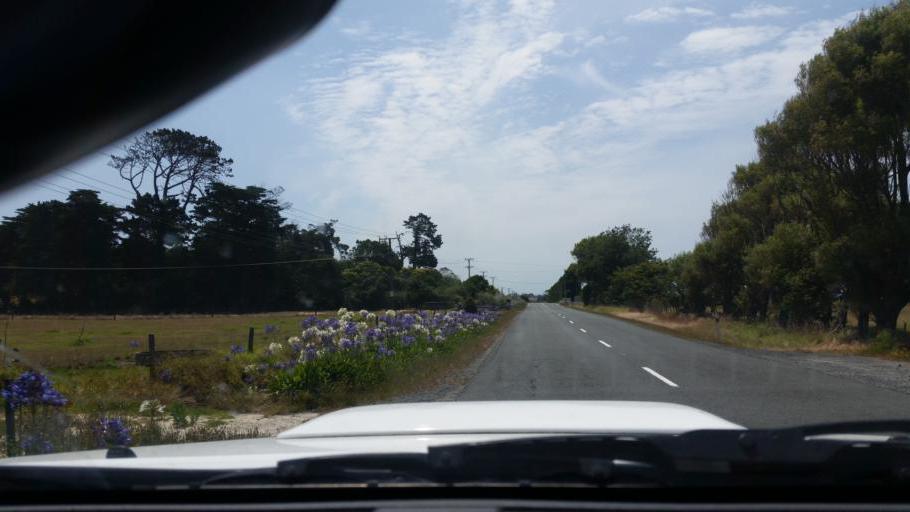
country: NZ
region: Northland
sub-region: Kaipara District
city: Dargaville
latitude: -36.0612
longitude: 173.9364
